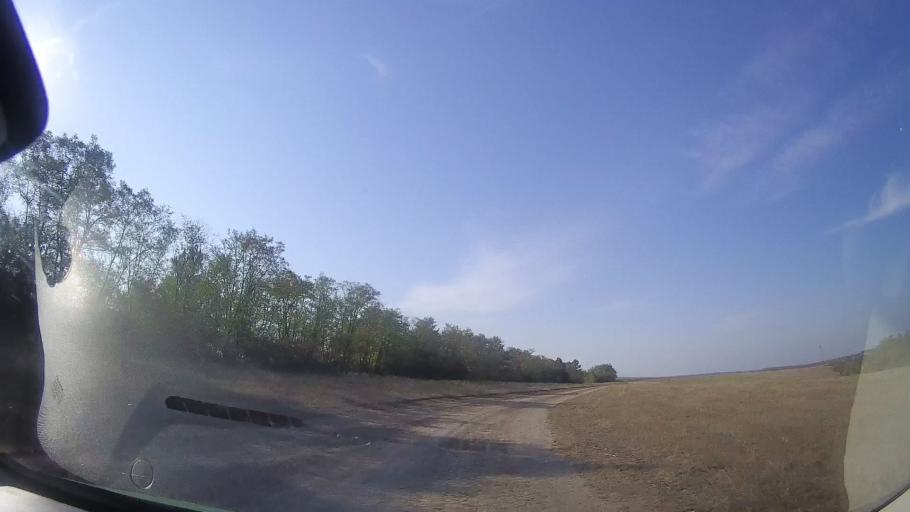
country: RO
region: Timis
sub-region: Comuna Bogda
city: Bogda
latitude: 45.8872
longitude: 21.5583
